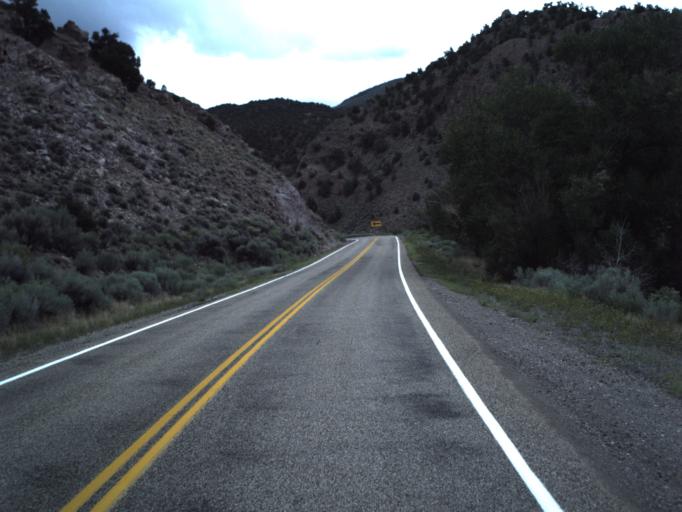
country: US
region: Utah
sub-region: Piute County
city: Junction
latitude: 38.1944
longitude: -112.1350
